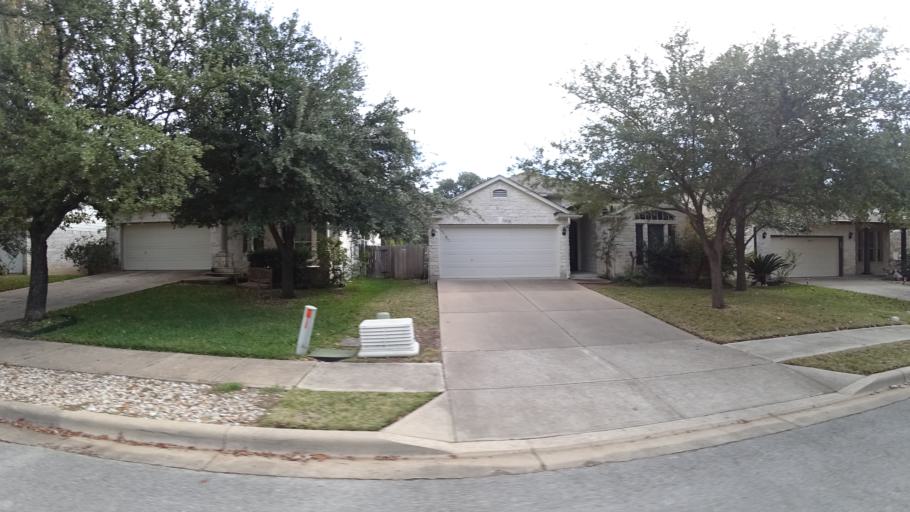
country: US
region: Texas
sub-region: Williamson County
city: Brushy Creek
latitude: 30.5066
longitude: -97.7461
